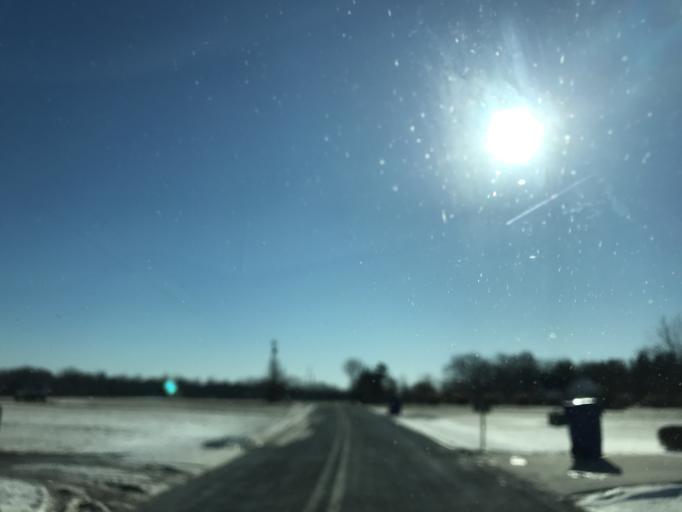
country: US
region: Maryland
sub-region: Charles County
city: La Plata
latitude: 38.4349
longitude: -76.9164
